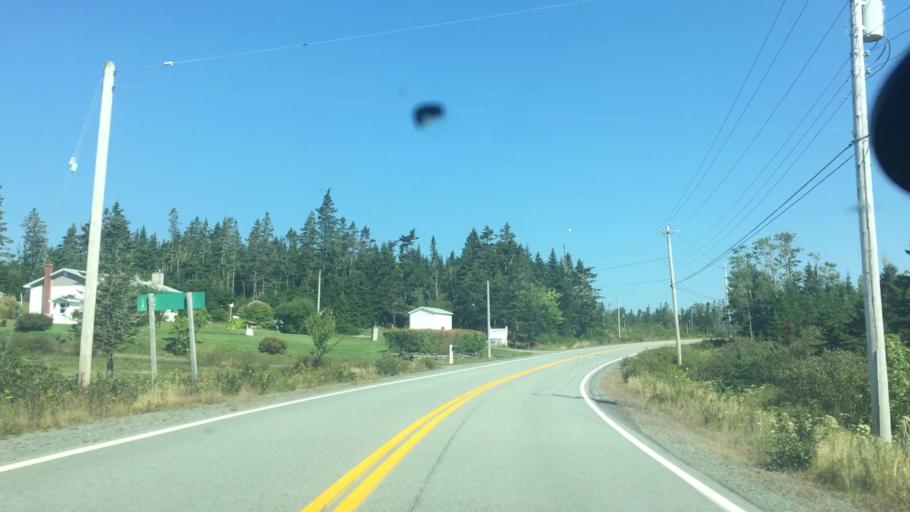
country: CA
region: Nova Scotia
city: New Glasgow
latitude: 44.9275
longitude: -62.2984
